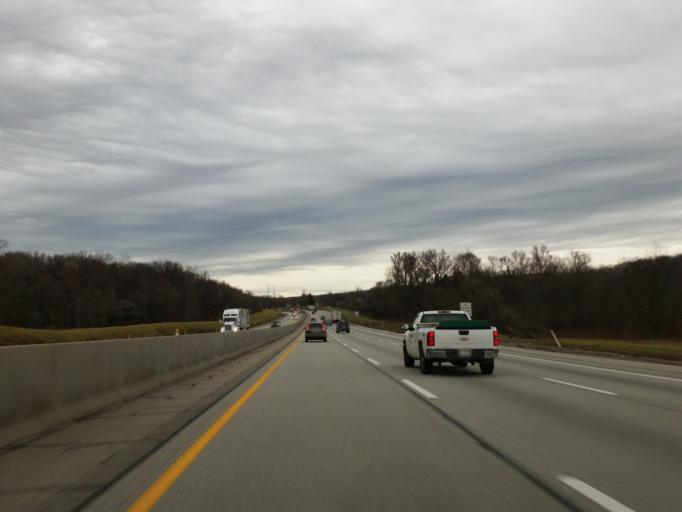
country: US
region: Pennsylvania
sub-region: Westmoreland County
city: Ligonier
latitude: 40.1228
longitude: -79.3102
